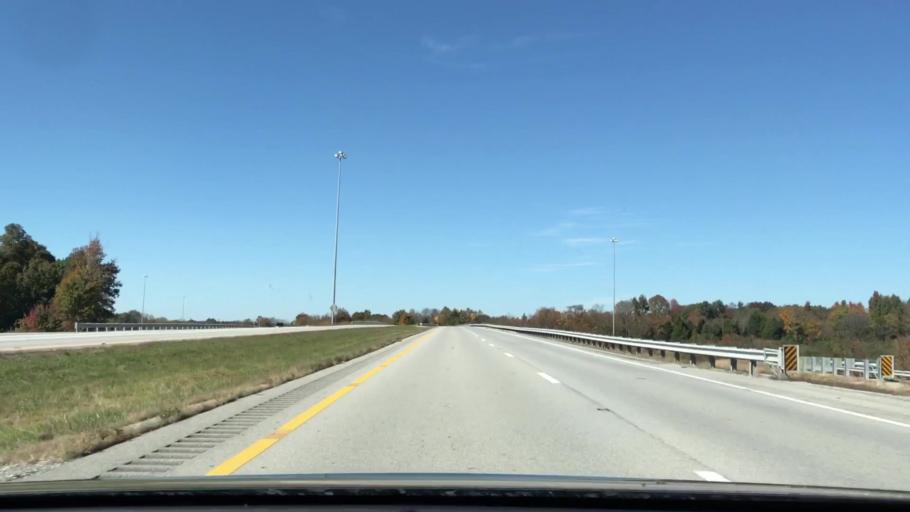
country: US
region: Kentucky
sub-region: Barren County
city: Cave City
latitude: 37.0567
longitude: -86.1086
